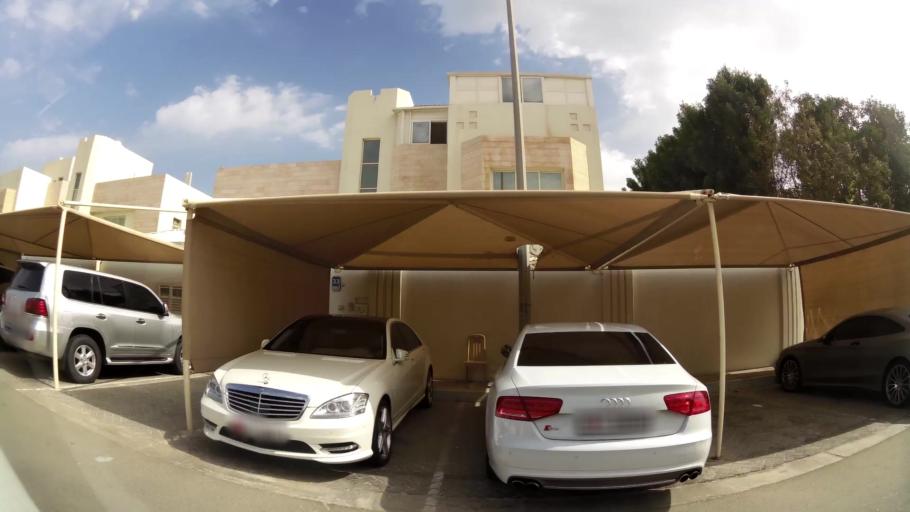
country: AE
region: Abu Dhabi
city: Abu Dhabi
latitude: 24.4334
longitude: 54.3706
